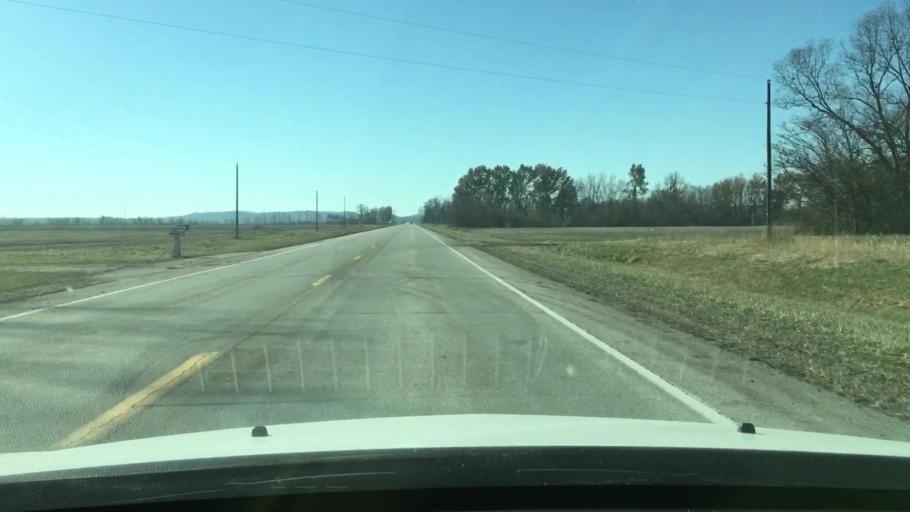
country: US
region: Missouri
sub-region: Pike County
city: Louisiana
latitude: 39.4959
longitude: -91.0032
